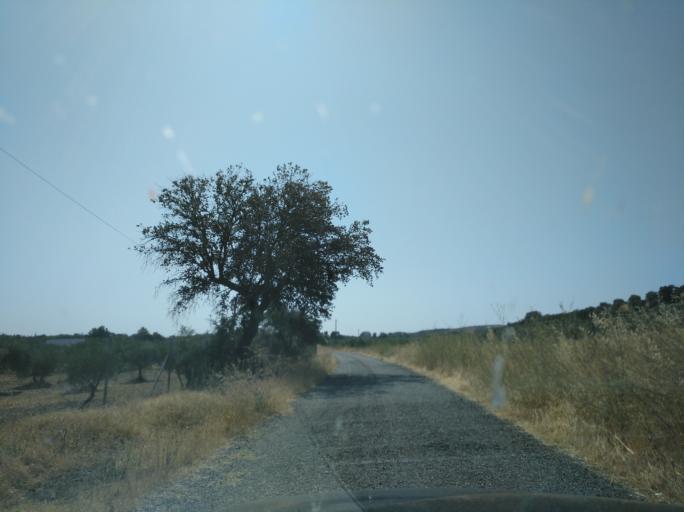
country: PT
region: Portalegre
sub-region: Campo Maior
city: Campo Maior
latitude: 39.0767
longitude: -7.0196
